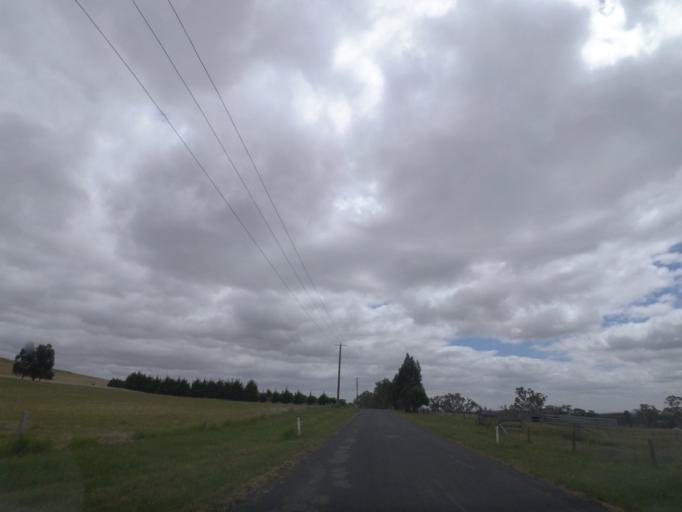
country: AU
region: Victoria
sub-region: Whittlesea
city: Whittlesea
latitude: -37.1842
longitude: 145.0380
